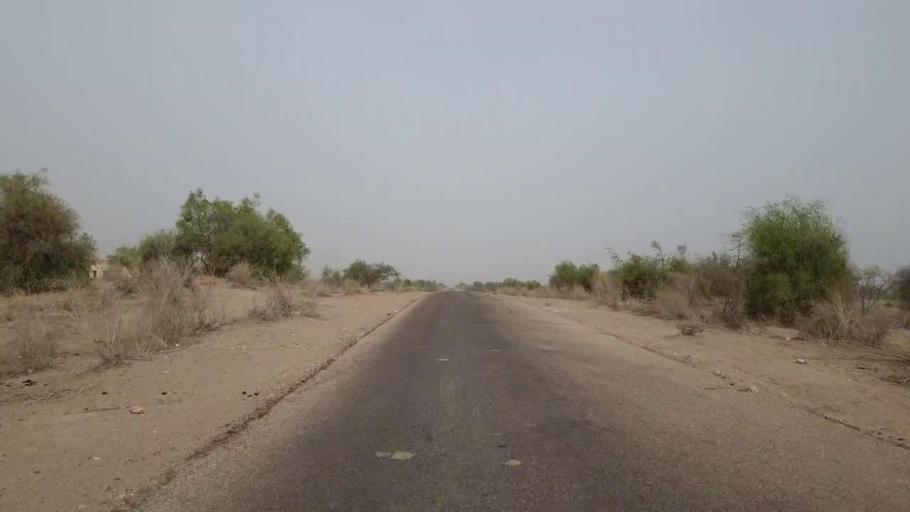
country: PK
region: Sindh
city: Islamkot
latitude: 24.5731
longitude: 70.3173
